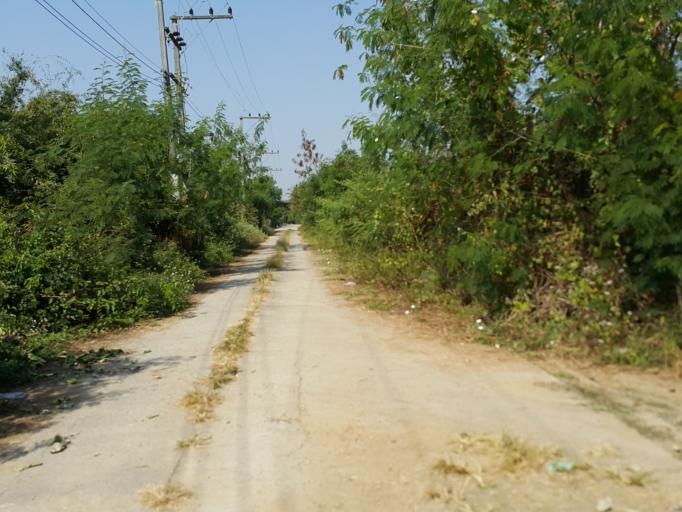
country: TH
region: Chiang Mai
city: San Kamphaeng
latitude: 18.7812
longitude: 99.1015
